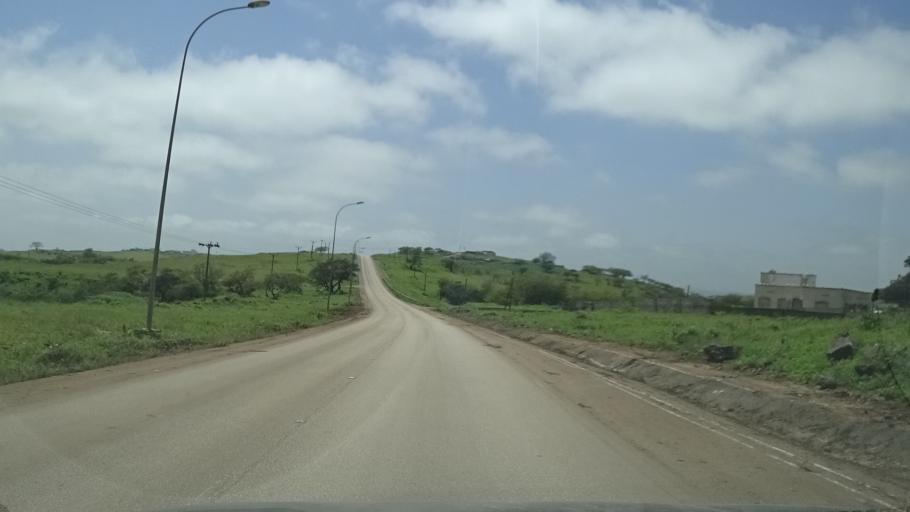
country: OM
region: Zufar
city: Salalah
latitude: 17.2211
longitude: 54.2595
